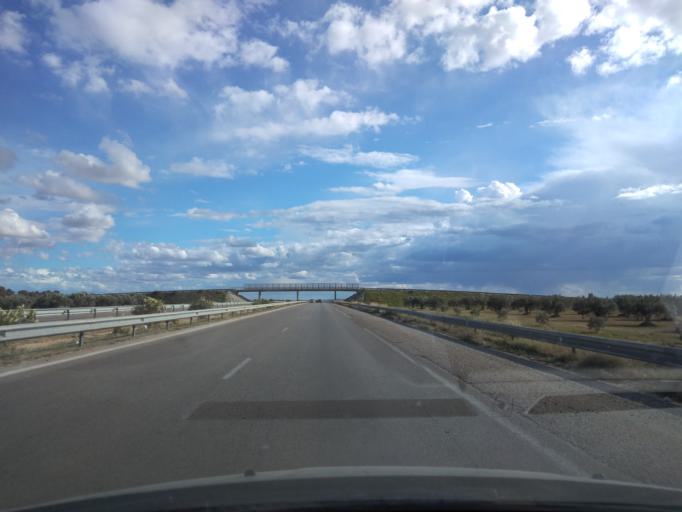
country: TN
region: Al Munastir
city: Manzil Kamil
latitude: 35.6205
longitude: 10.5943
